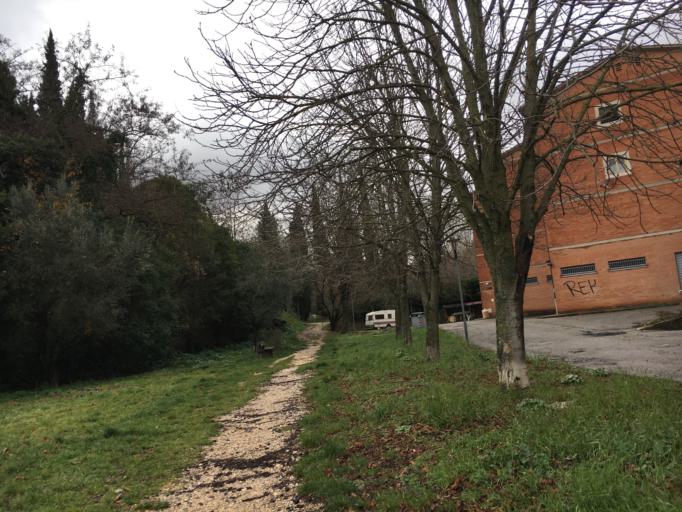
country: IT
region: Umbria
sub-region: Provincia di Perugia
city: Perugia
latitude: 43.1185
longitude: 12.3727
